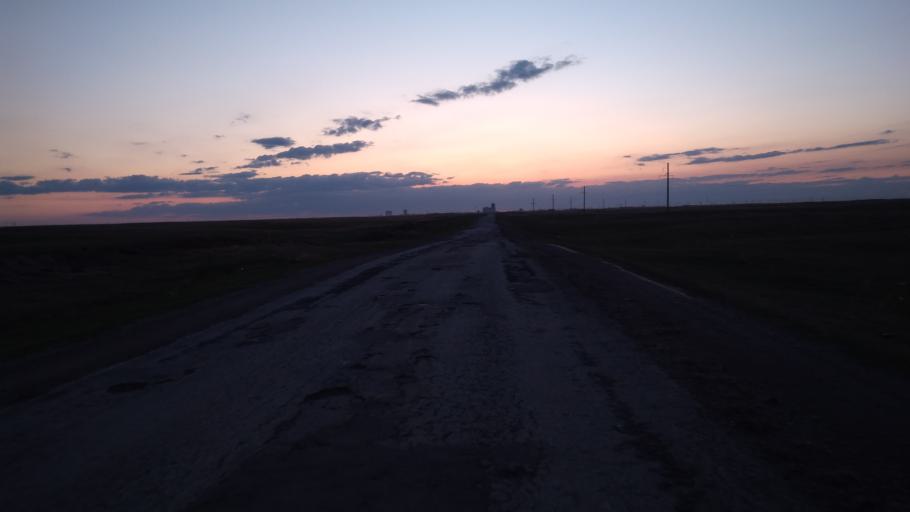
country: RU
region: Chelyabinsk
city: Troitsk
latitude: 54.0897
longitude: 61.6490
